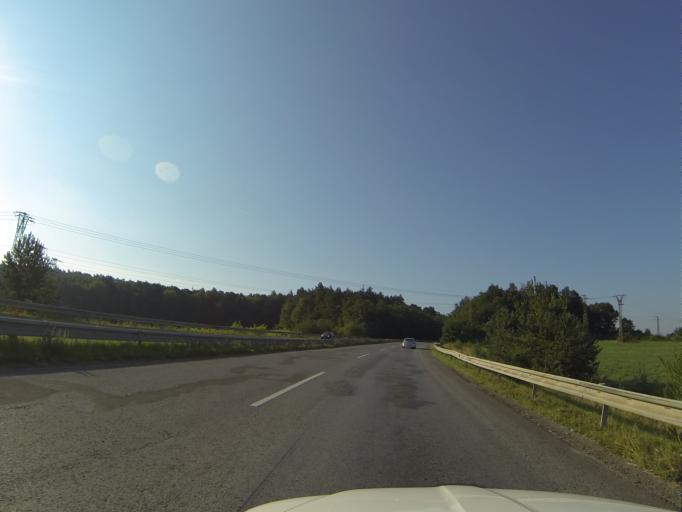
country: SK
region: Nitriansky
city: Prievidza
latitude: 48.7537
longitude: 18.6273
